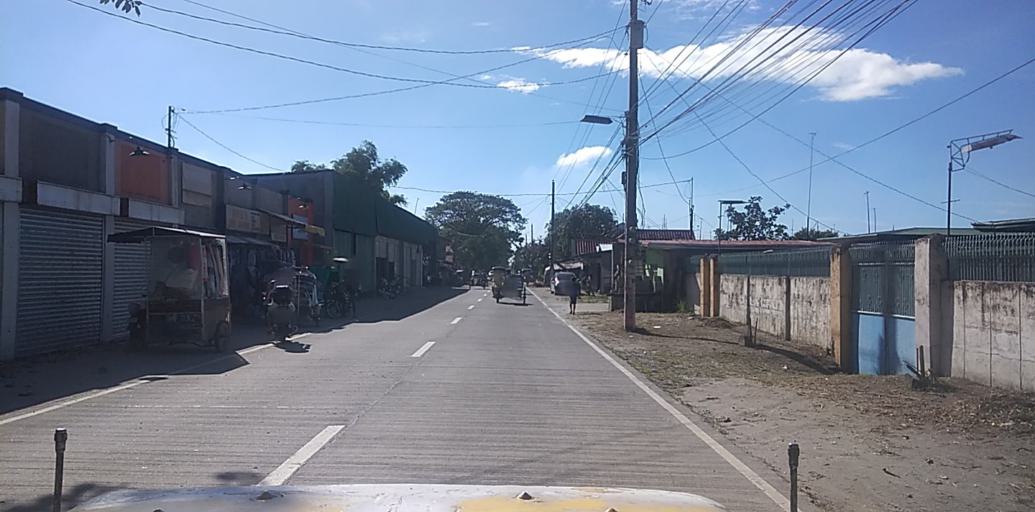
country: PH
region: Central Luzon
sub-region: Province of Pampanga
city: San Patricio
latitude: 15.0903
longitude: 120.7130
